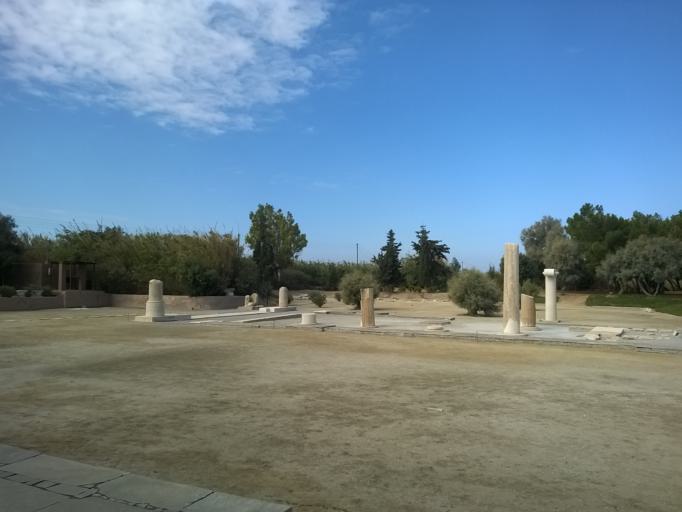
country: GR
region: South Aegean
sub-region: Nomos Kykladon
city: Naxos
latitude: 37.0777
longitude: 25.3811
